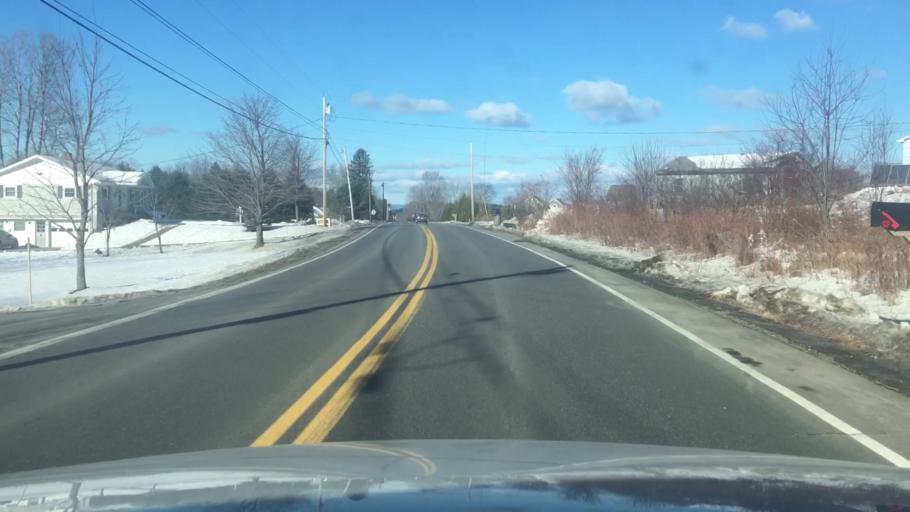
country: US
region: Maine
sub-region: Somerset County
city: Skowhegan
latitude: 44.7373
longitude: -69.6840
